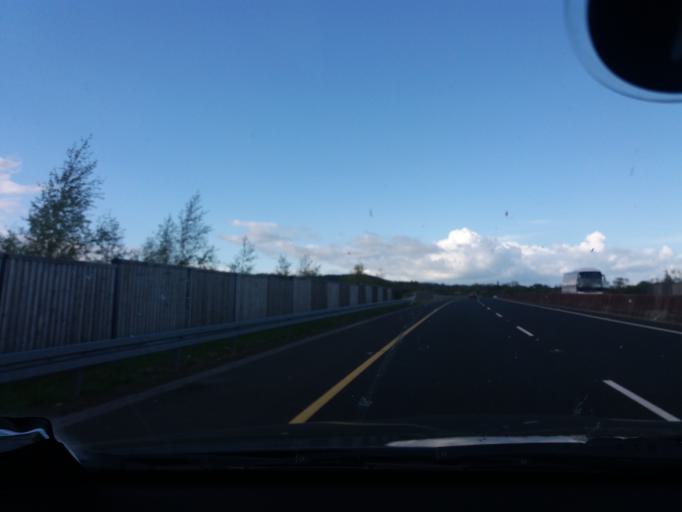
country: IE
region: Leinster
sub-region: Kilkenny
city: Thomastown
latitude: 52.6472
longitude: -7.1044
